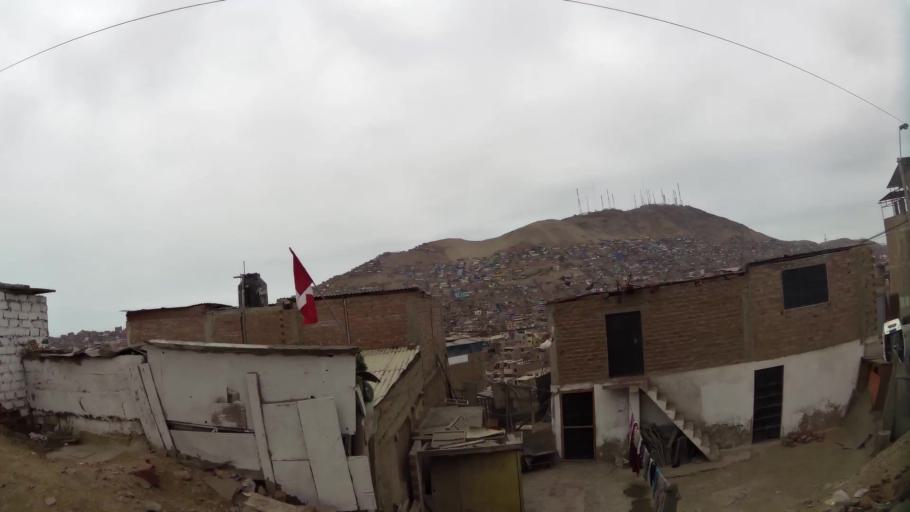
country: PE
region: Lima
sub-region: Lima
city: Surco
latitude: -12.1861
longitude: -77.0135
